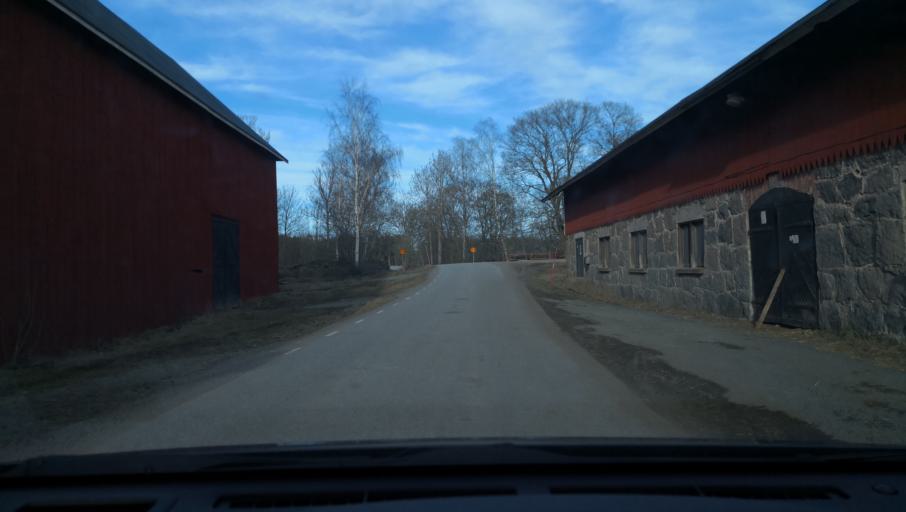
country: SE
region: Uppsala
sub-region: Enkopings Kommun
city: Grillby
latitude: 59.5437
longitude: 17.2044
